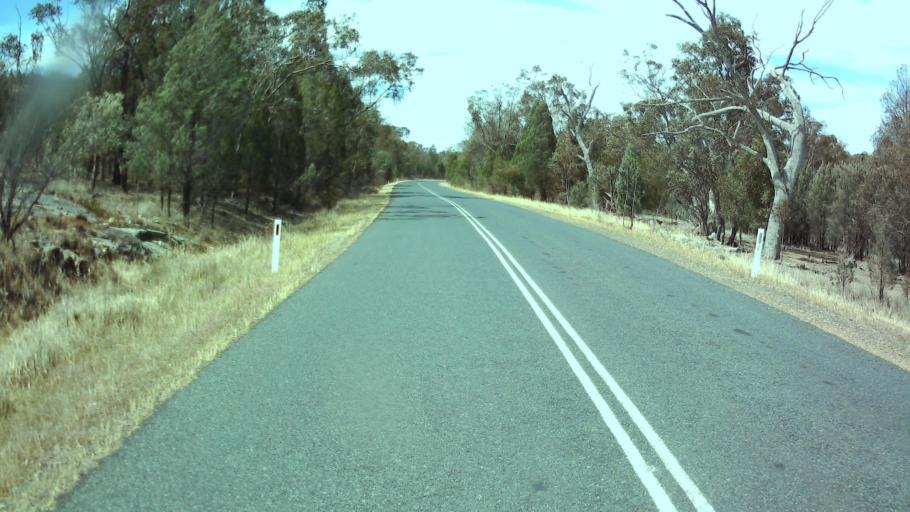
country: AU
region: New South Wales
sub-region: Weddin
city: Grenfell
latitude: -33.6780
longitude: 148.2832
